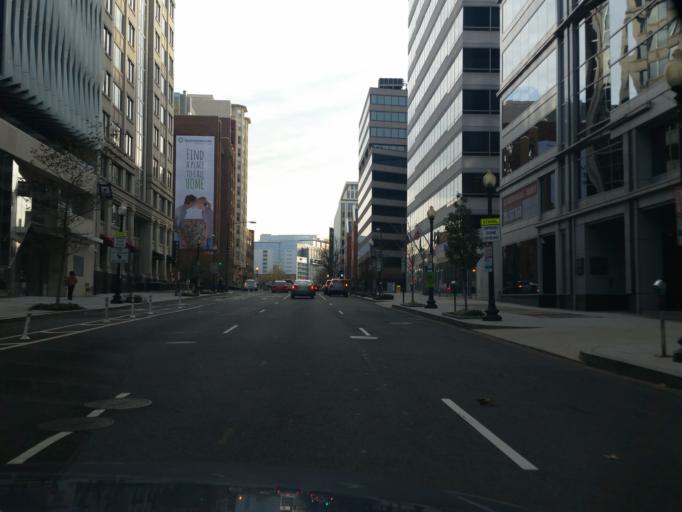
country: US
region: Washington, D.C.
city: Washington, D.C.
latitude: 38.9037
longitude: -77.0308
